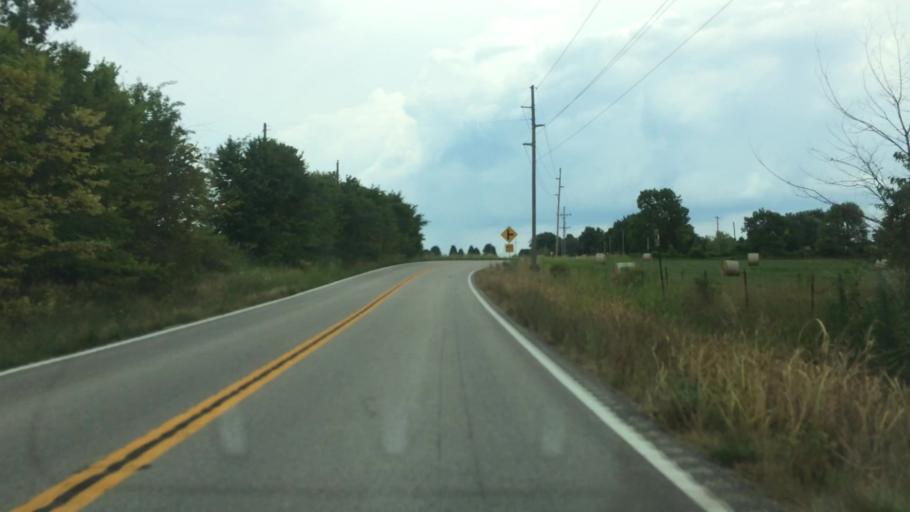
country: US
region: Missouri
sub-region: Greene County
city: Strafford
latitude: 37.2423
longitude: -93.1361
